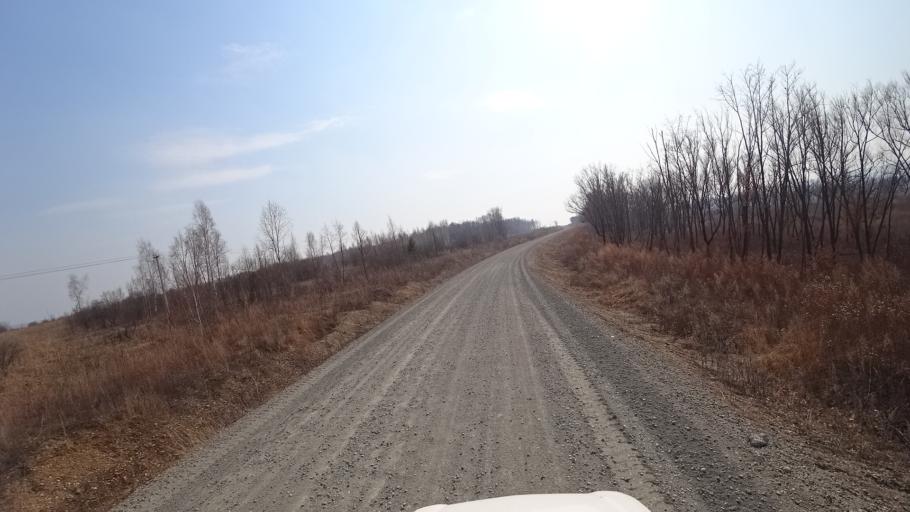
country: RU
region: Amur
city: Novobureyskiy
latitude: 49.8242
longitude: 129.9862
